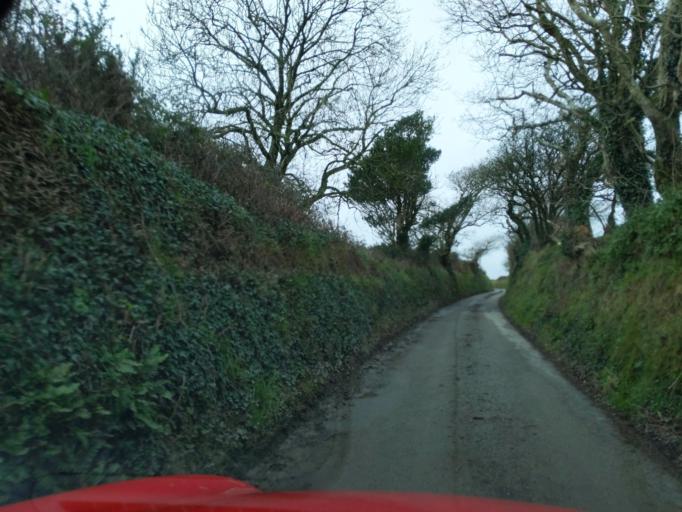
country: GB
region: England
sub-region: Cornwall
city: Duloe
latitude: 50.3488
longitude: -4.5448
